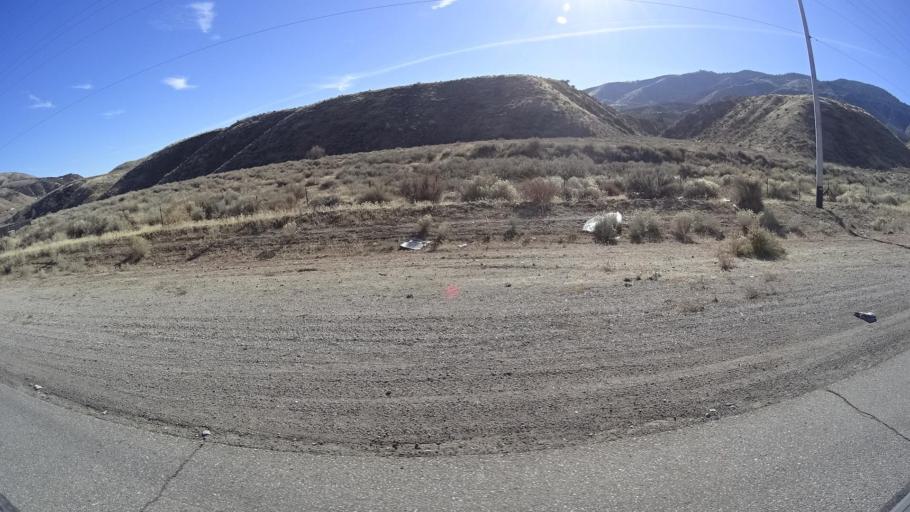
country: US
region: California
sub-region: Kern County
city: Lebec
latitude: 34.8184
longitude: -118.8974
